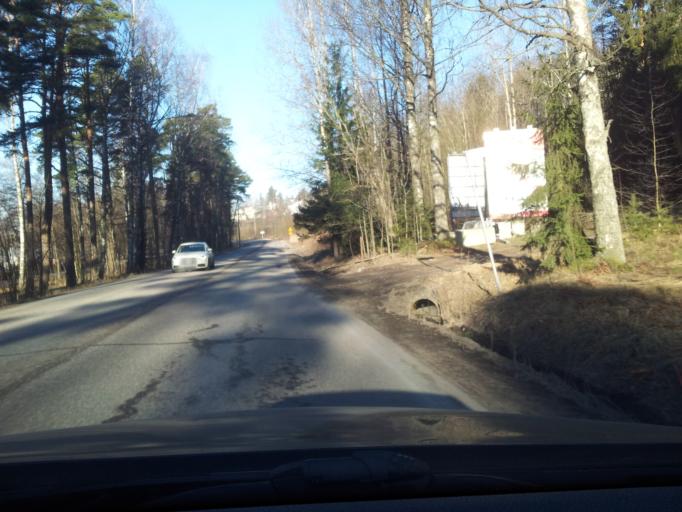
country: FI
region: Uusimaa
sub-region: Helsinki
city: Espoo
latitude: 60.1573
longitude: 24.6227
